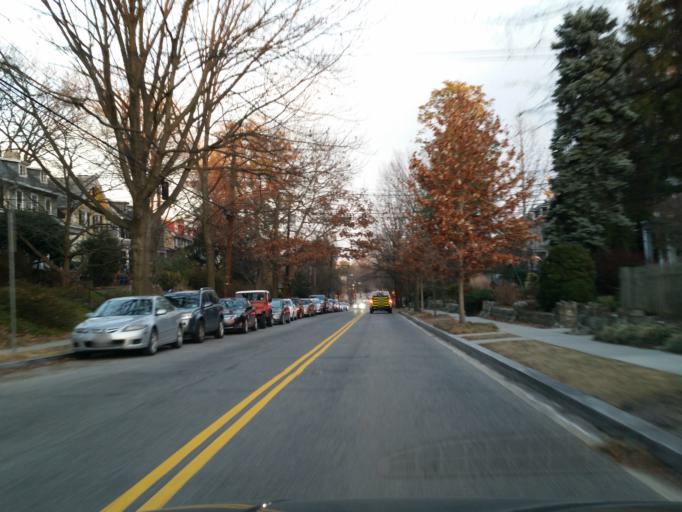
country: US
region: Maryland
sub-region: Montgomery County
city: Chevy Chase Village
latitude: 38.9649
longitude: -77.0791
